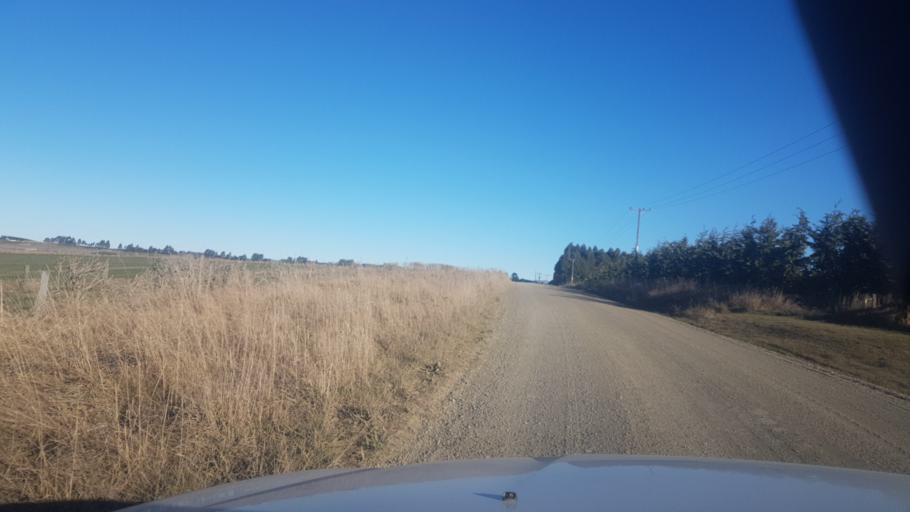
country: NZ
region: Canterbury
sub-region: Timaru District
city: Pleasant Point
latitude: -44.3475
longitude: 171.0743
